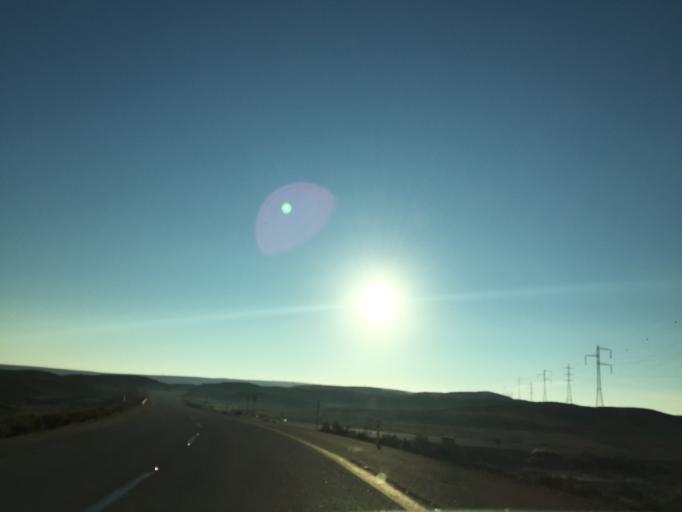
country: IL
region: Southern District
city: Mitzpe Ramon
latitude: 30.5308
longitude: 34.9200
